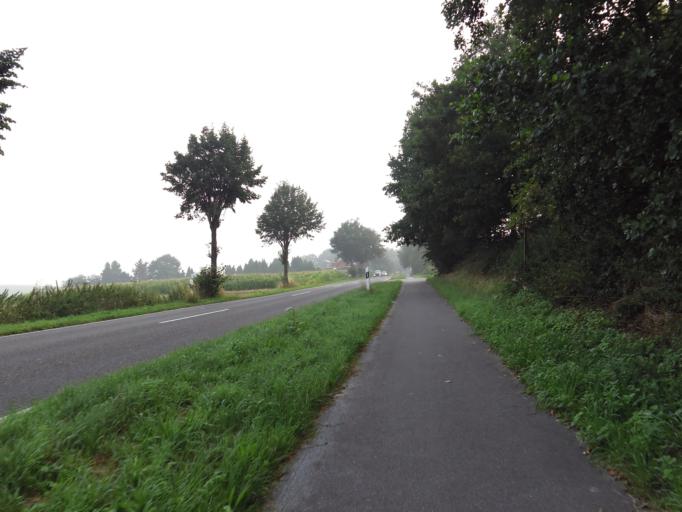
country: DE
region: North Rhine-Westphalia
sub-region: Regierungsbezirk Koln
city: Herzogenrath
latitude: 50.8945
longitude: 6.1074
